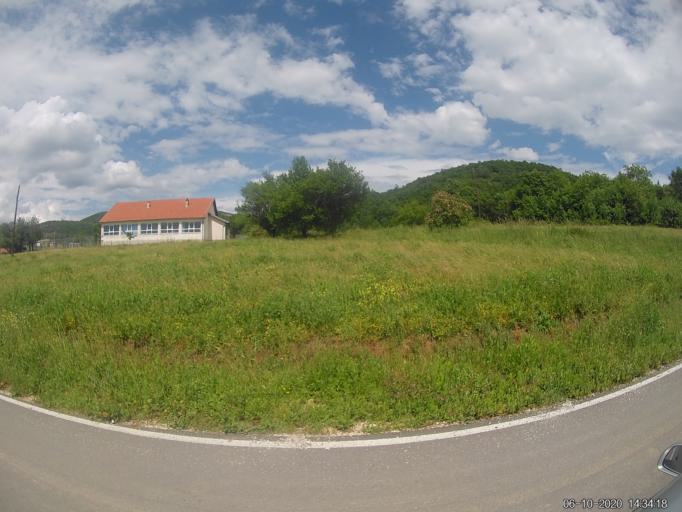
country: XK
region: Prizren
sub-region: Komuna e Therandes
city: Budakovo
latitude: 42.4154
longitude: 20.9298
